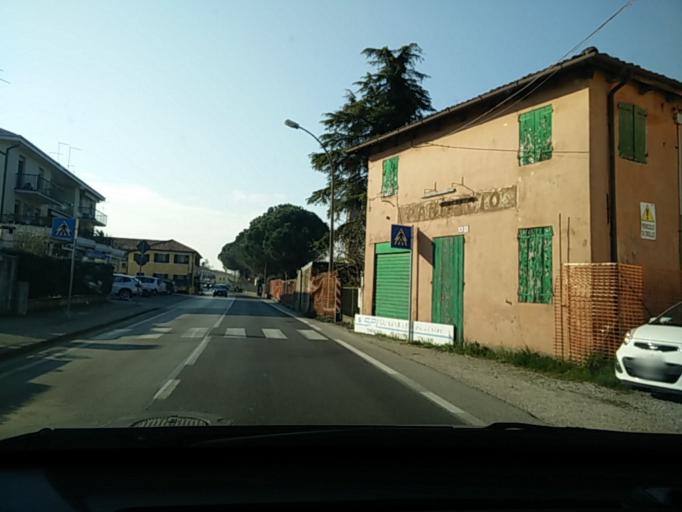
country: IT
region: Veneto
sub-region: Provincia di Treviso
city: Breda
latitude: 45.7221
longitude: 12.3314
